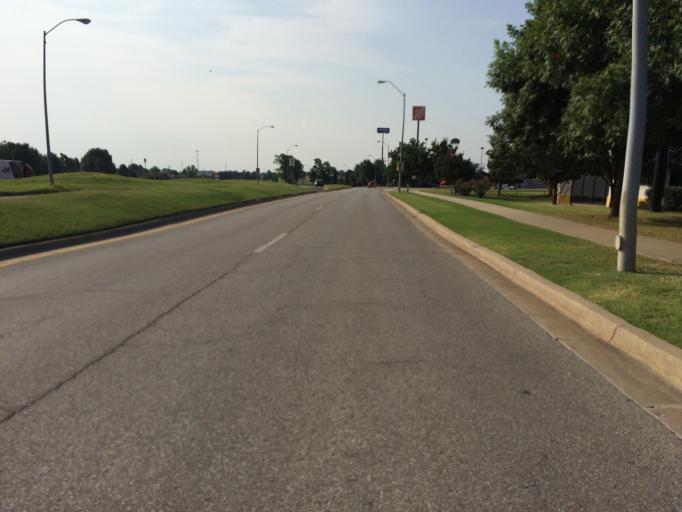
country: US
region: Oklahoma
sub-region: Cleveland County
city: Norman
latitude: 35.2103
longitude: -97.4835
